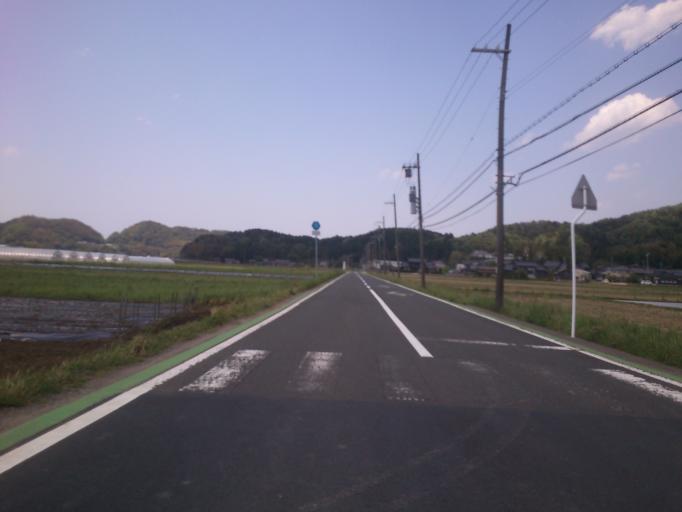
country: JP
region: Kyoto
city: Miyazu
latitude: 35.7191
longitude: 135.1081
